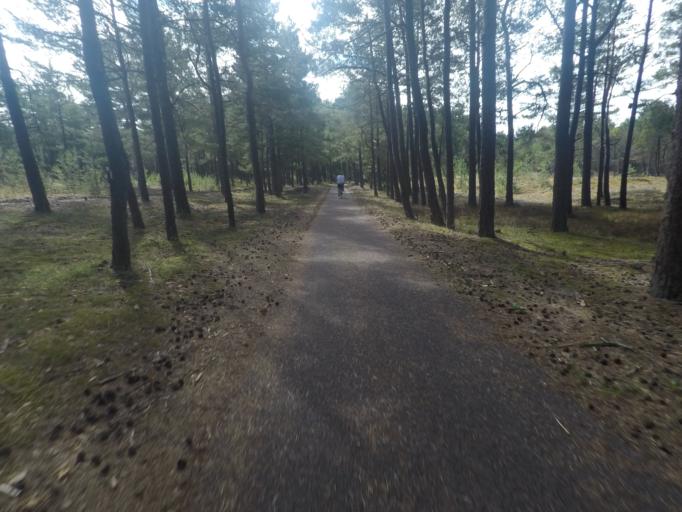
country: LT
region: Klaipedos apskritis
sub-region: Klaipeda
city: Klaipeda
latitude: 55.5620
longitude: 21.1138
